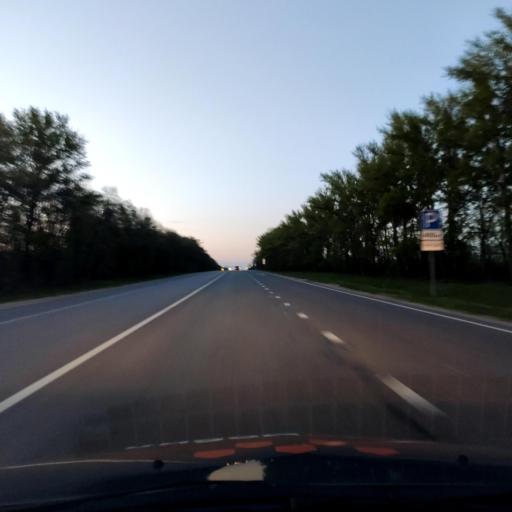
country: RU
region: Orjol
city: Zmiyevka
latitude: 52.7091
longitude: 36.3569
